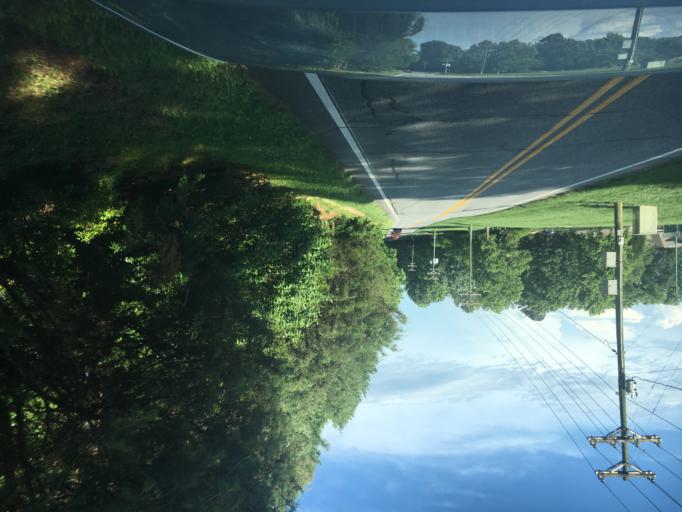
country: US
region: South Carolina
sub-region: Greenville County
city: Five Forks
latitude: 34.7879
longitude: -82.2387
